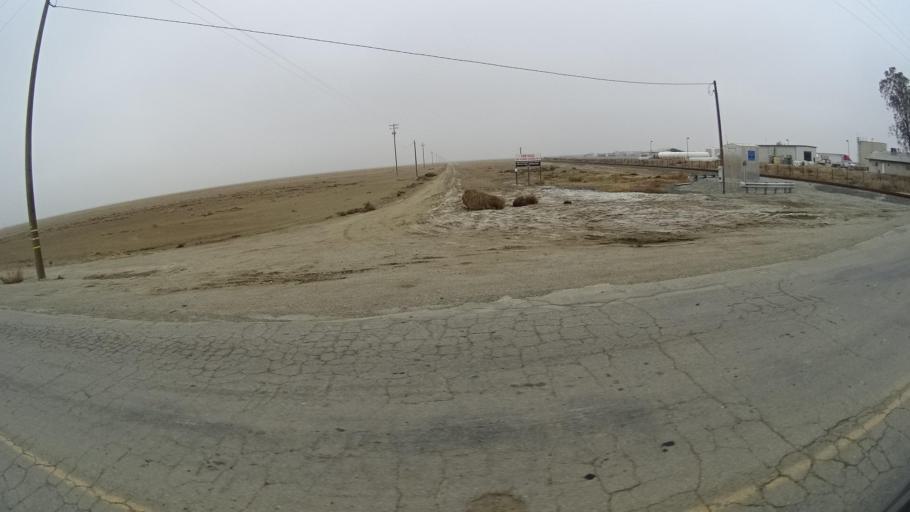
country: US
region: California
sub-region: Kern County
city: Maricopa
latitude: 35.1519
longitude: -119.2347
